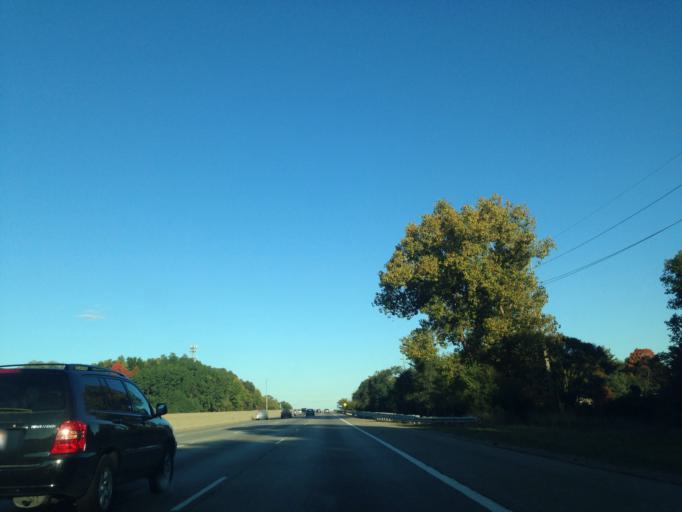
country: US
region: Michigan
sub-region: Oakland County
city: Farmington Hills
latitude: 42.4935
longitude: -83.4037
